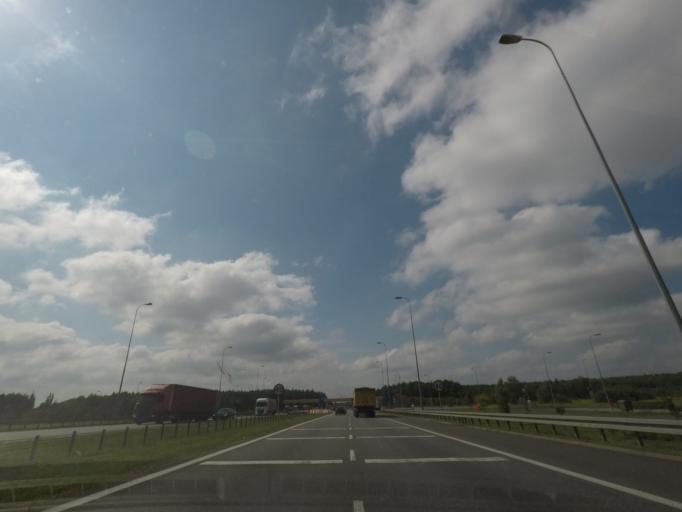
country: PL
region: Kujawsko-Pomorskie
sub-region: Powiat torunski
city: Lubicz Dolny
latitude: 53.0118
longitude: 18.7350
